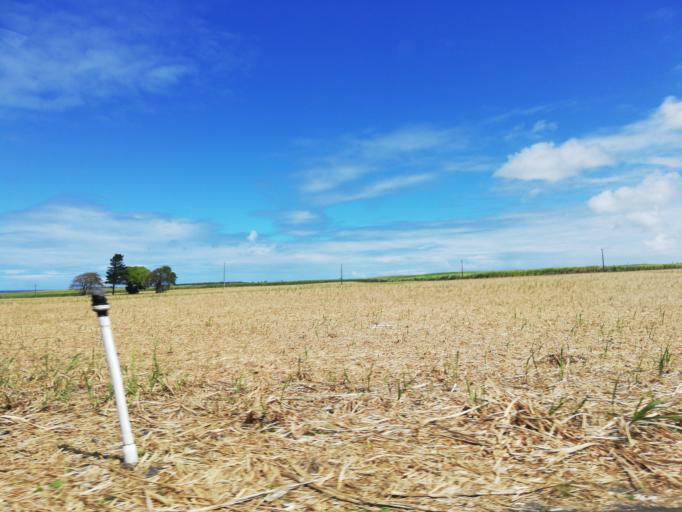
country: MU
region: Grand Port
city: Plaine Magnien
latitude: -20.4616
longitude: 57.6573
